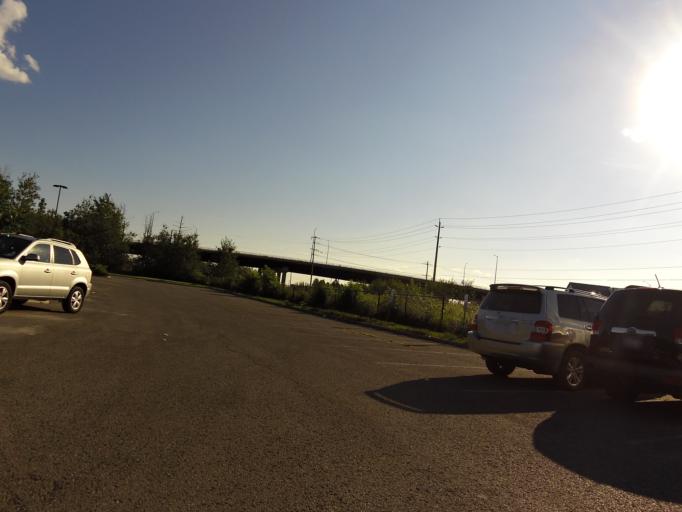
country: CA
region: Ontario
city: Ottawa
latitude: 45.3395
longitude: -75.7056
